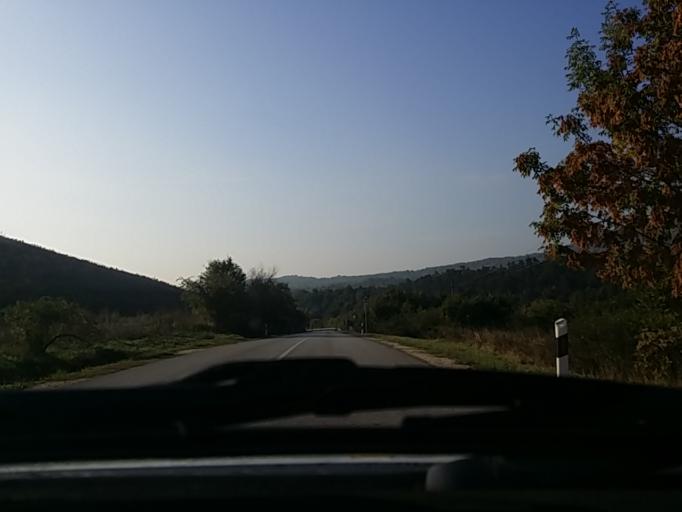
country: HU
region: Pest
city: Nagykovacsi
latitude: 47.6940
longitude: 19.0333
